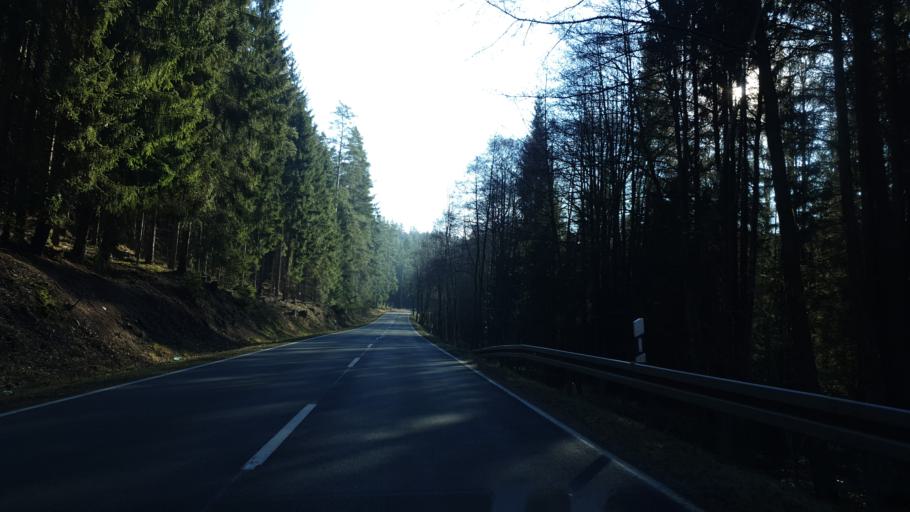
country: DE
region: Saxony
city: Bad Brambach
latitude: 50.2452
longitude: 12.3018
